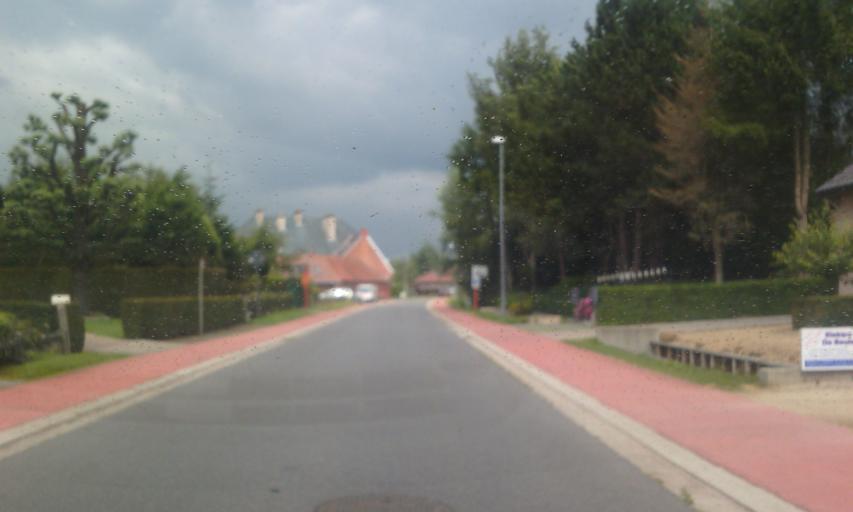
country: BE
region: Flanders
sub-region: Provincie Oost-Vlaanderen
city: Lokeren
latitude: 51.1041
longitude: 3.9606
